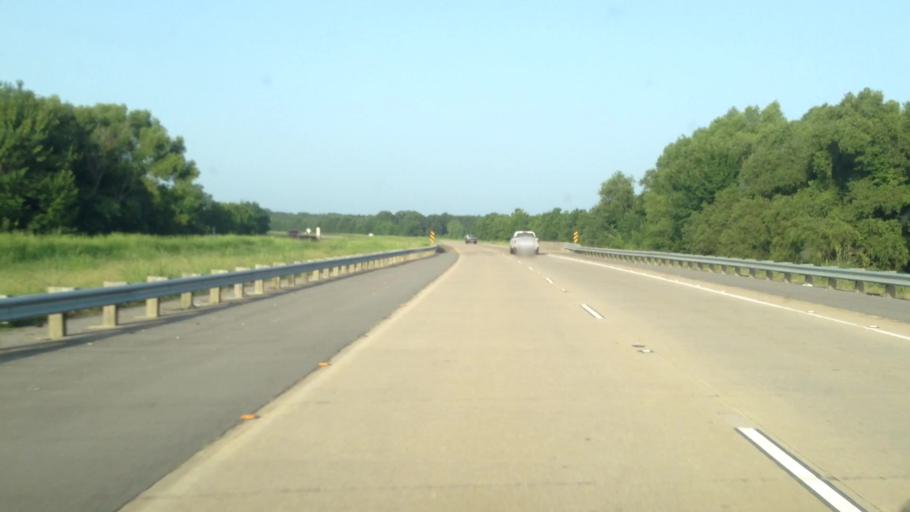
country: US
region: Louisiana
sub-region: Rapides Parish
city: Alexandria
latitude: 31.2354
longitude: -92.4575
